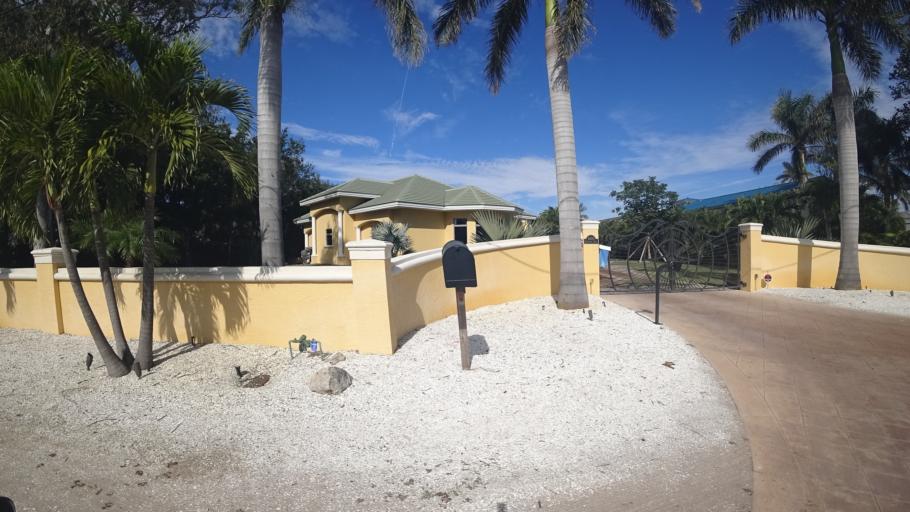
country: US
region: Florida
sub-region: Manatee County
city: West Bradenton
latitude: 27.5122
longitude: -82.6256
